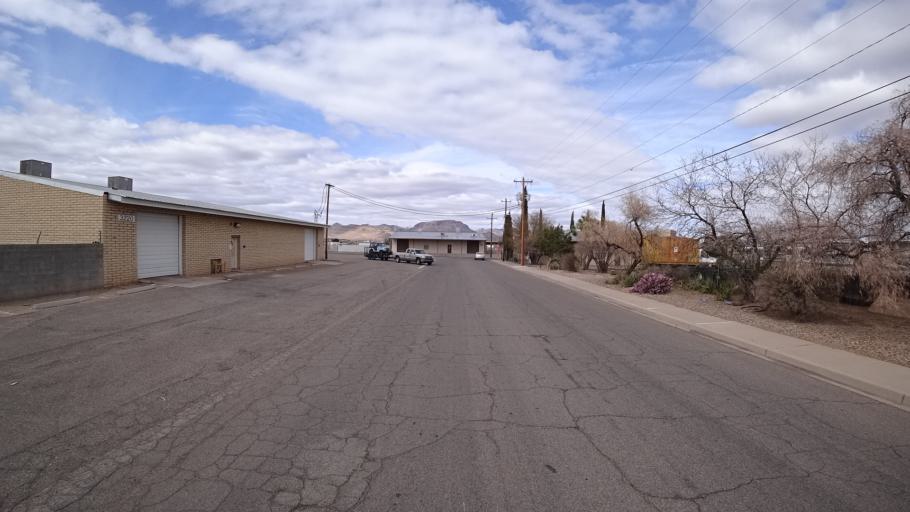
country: US
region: Arizona
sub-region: Mohave County
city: New Kingman-Butler
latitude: 35.2299
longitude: -114.0002
